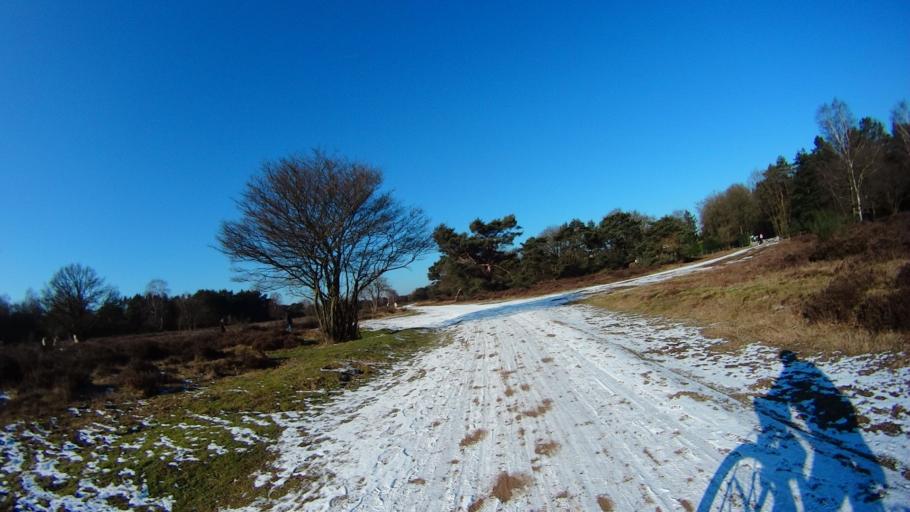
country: NL
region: North Holland
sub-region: Gemeente Laren
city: Laren
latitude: 52.2404
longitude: 5.2141
